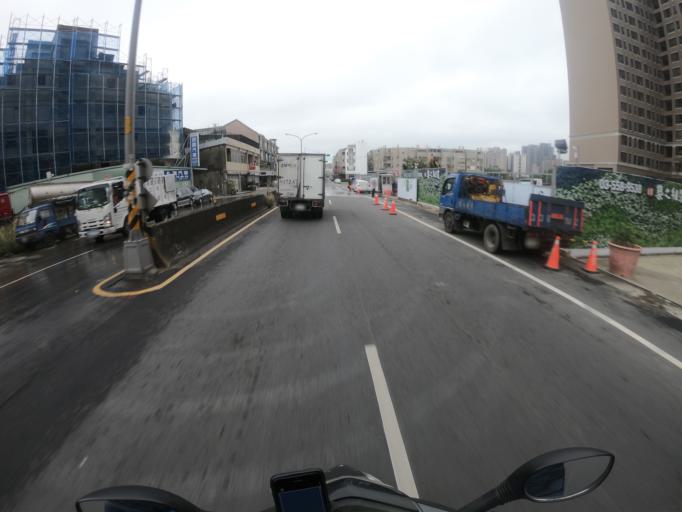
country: TW
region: Taiwan
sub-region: Hsinchu
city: Zhubei
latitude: 24.8265
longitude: 121.0042
